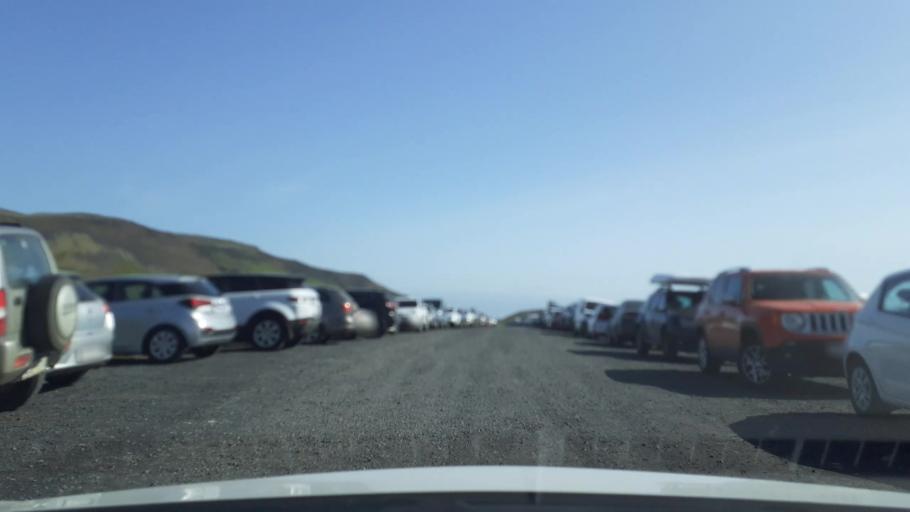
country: IS
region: South
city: Hveragerdi
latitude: 64.0216
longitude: -21.2107
